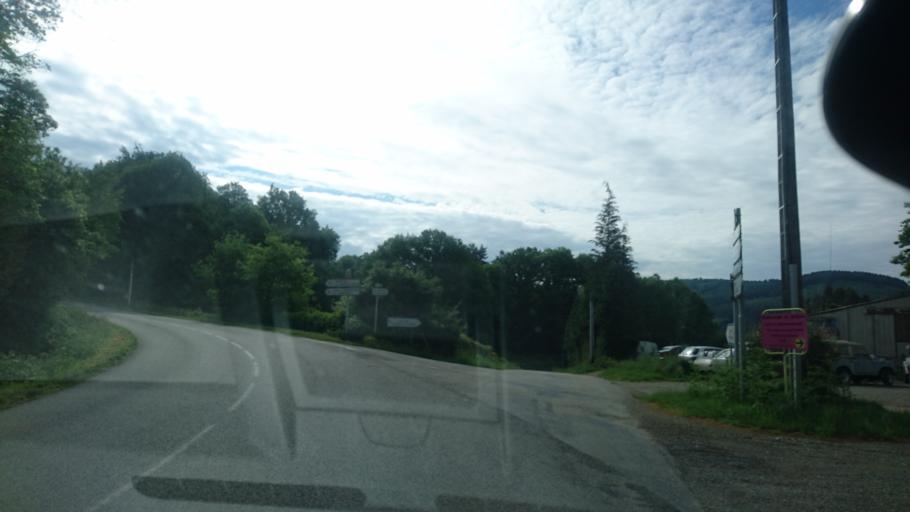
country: FR
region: Limousin
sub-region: Departement de la Haute-Vienne
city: Peyrat-le-Chateau
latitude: 45.8099
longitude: 1.7889
